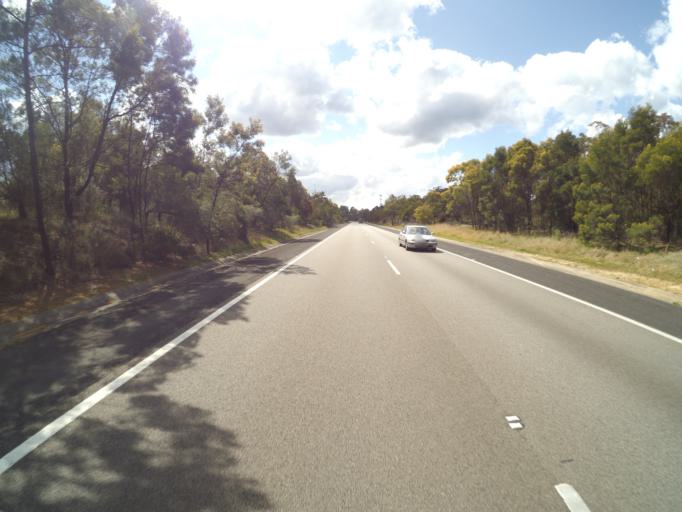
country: AU
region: New South Wales
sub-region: Wingecarribee
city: Colo Vale
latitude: -34.3733
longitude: 150.5334
